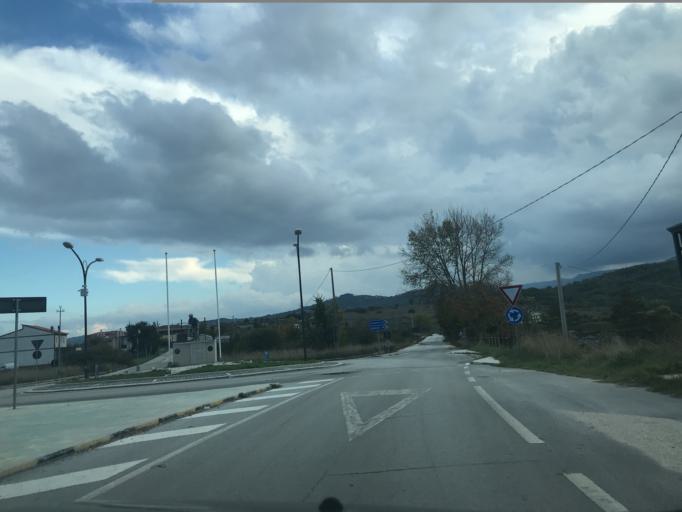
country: IT
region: Molise
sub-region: Provincia di Isernia
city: Bagnoli del Trigno
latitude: 41.6971
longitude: 14.4606
